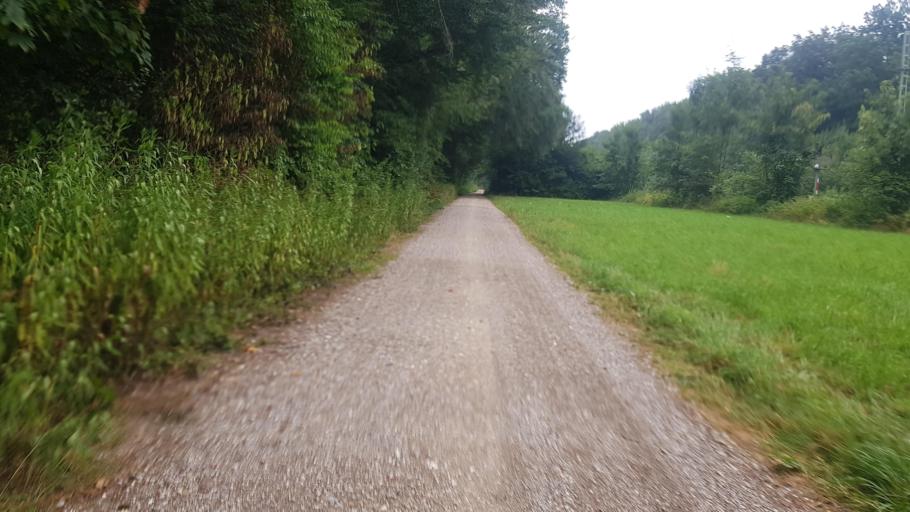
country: DE
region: Bavaria
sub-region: Upper Bavaria
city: Gauting
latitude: 48.0414
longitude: 11.3585
